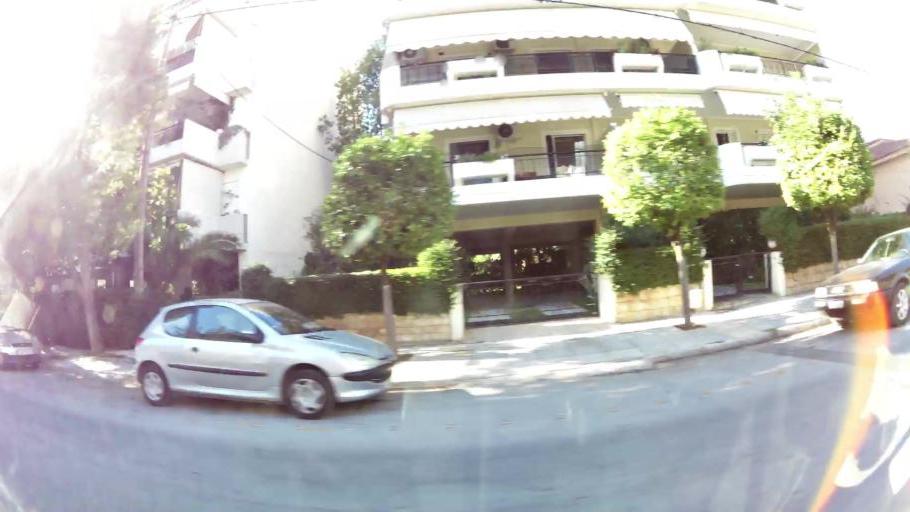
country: GR
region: Attica
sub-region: Nomarchia Athinas
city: Vrilissia
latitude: 38.0296
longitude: 23.8337
